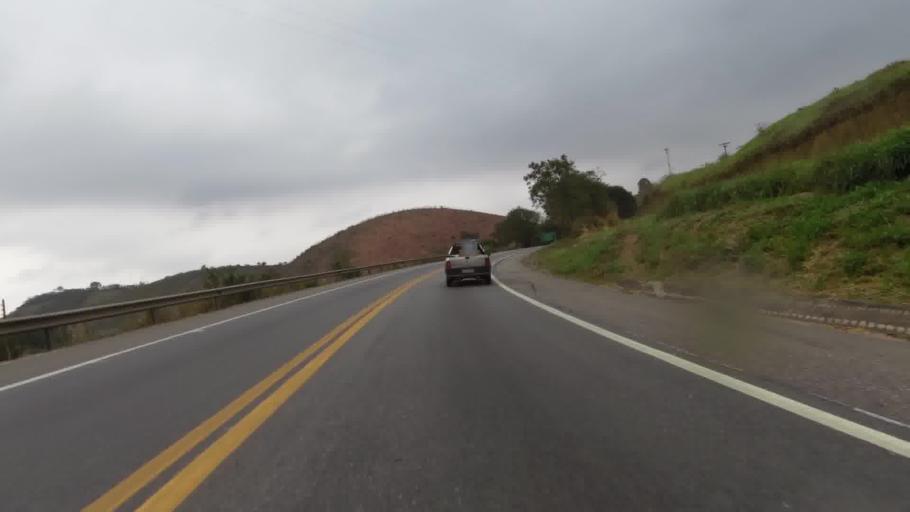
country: BR
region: Espirito Santo
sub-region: Rio Novo Do Sul
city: Rio Novo do Sul
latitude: -20.8892
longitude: -40.9859
